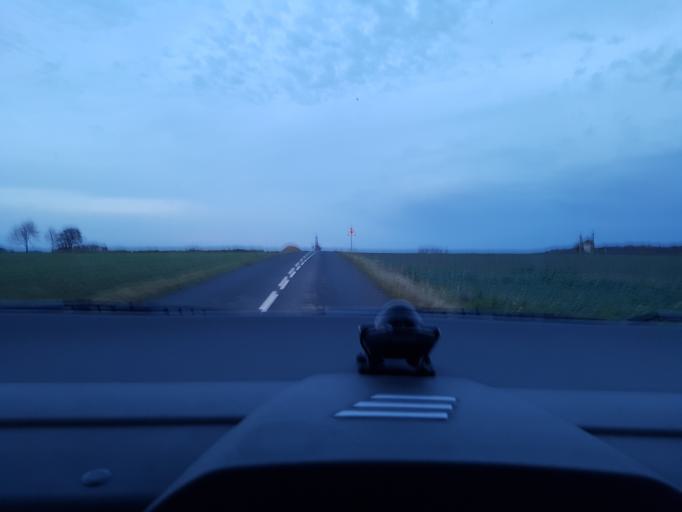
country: FR
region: Picardie
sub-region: Departement de la Somme
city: Beauquesne
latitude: 50.0712
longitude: 2.4204
